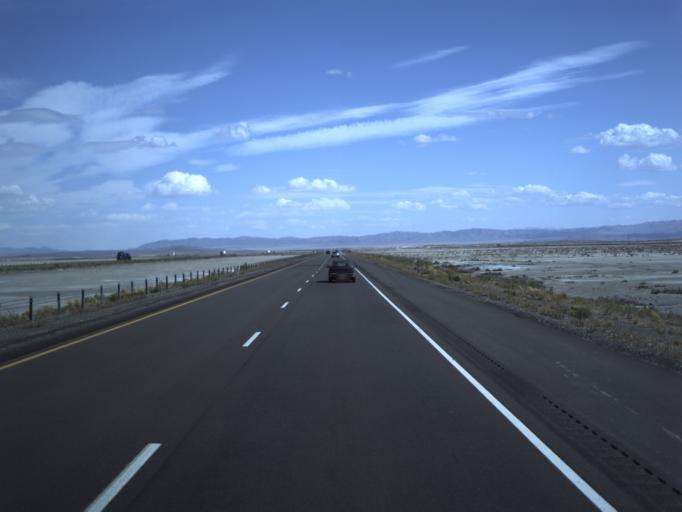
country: US
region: Utah
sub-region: Tooele County
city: Wendover
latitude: 40.7275
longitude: -113.3227
